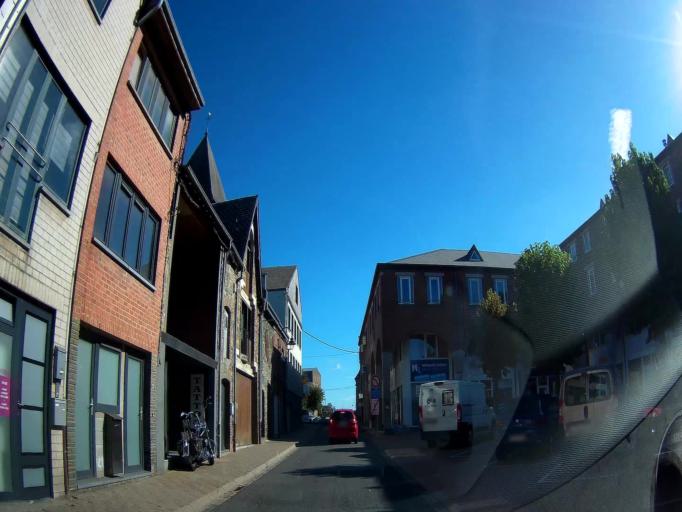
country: BE
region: Wallonia
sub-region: Province du Luxembourg
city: Bastogne
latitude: 50.0044
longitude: 5.7210
